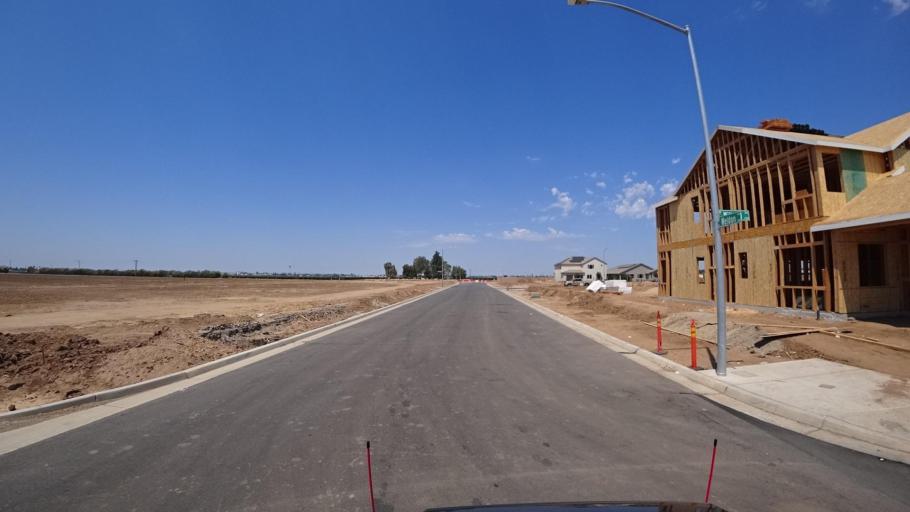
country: US
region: California
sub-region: Fresno County
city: Sunnyside
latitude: 36.7686
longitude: -119.6798
